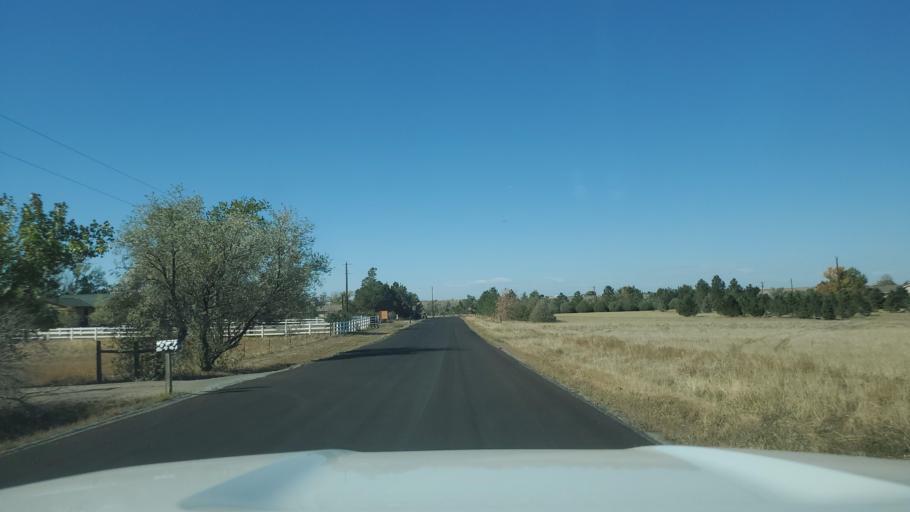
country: US
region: Colorado
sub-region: Adams County
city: Bennett
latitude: 39.7601
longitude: -104.3931
